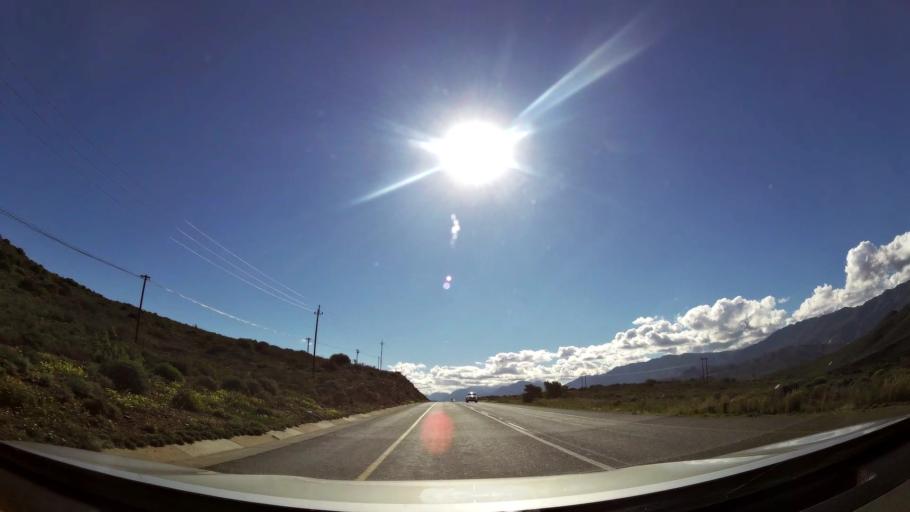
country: ZA
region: Western Cape
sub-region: Cape Winelands District Municipality
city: Ashton
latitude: -33.7868
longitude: 19.7728
